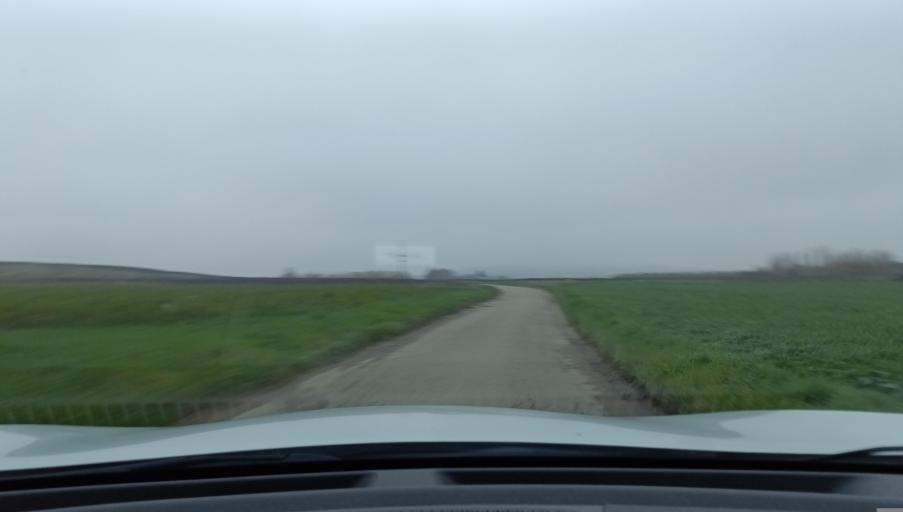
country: FR
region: Rhone-Alpes
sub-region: Departement de l'Isere
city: Seyssuel
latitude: 45.5798
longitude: 4.8488
